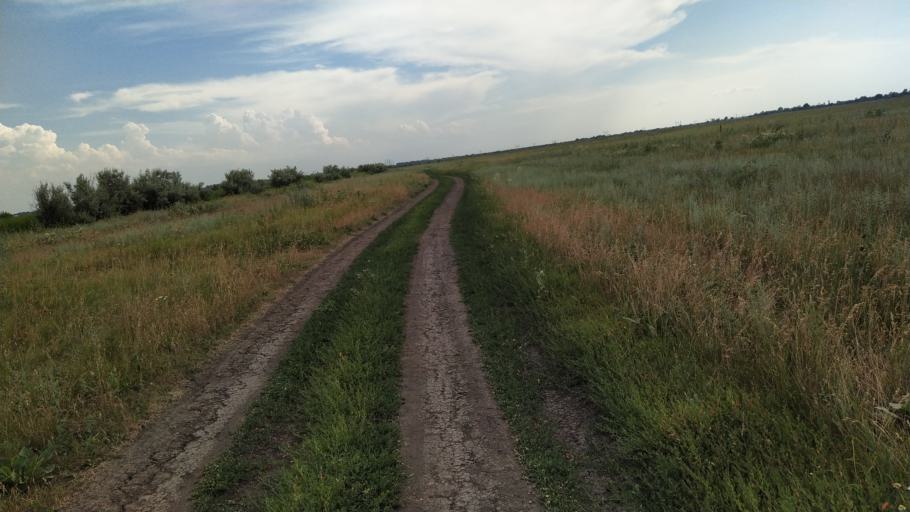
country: RU
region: Rostov
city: Kuleshovka
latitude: 47.1362
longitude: 39.6329
